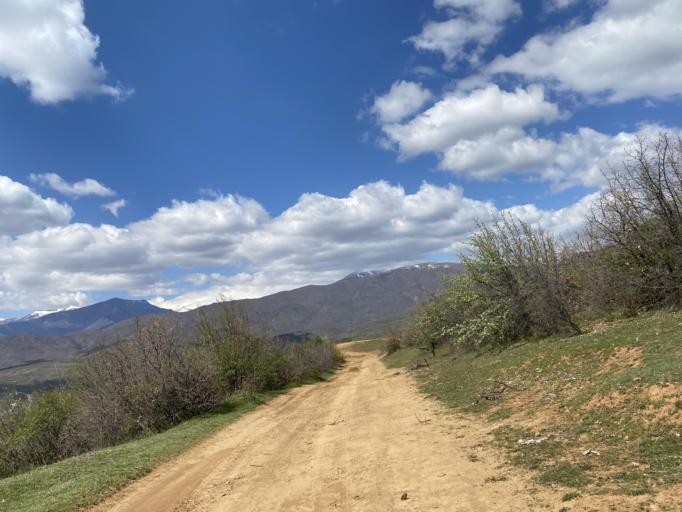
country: MK
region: Caska
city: Caska
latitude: 41.7284
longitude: 21.6630
